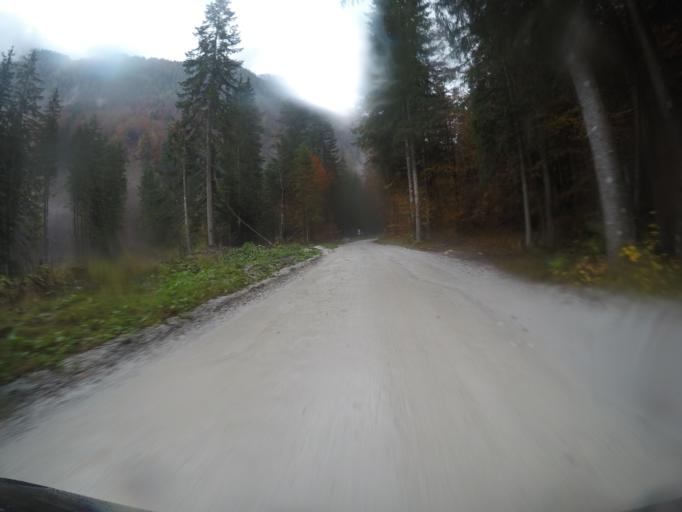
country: SI
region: Kranjska Gora
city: Mojstrana
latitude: 46.4417
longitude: 13.9014
